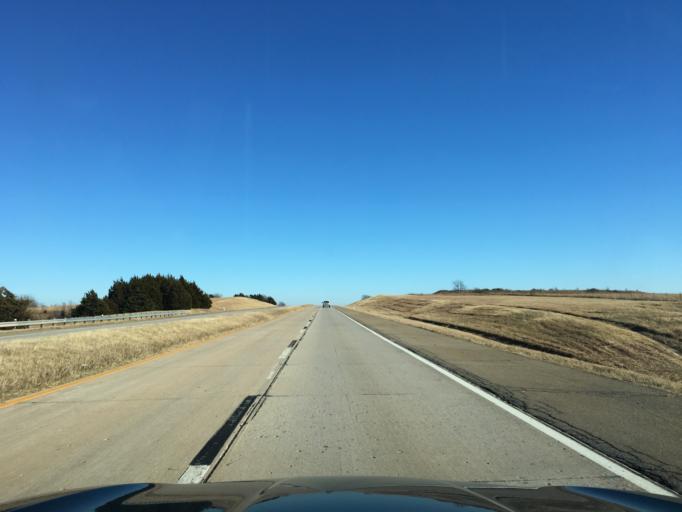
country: US
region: Oklahoma
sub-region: Payne County
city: Yale
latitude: 36.2240
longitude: -96.7364
